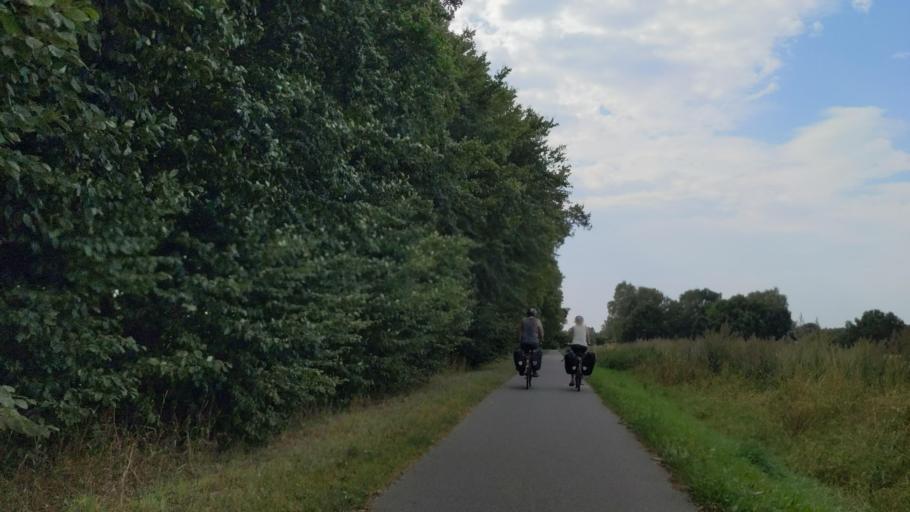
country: DE
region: Schleswig-Holstein
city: Gross Gronau
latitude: 53.8329
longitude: 10.7769
